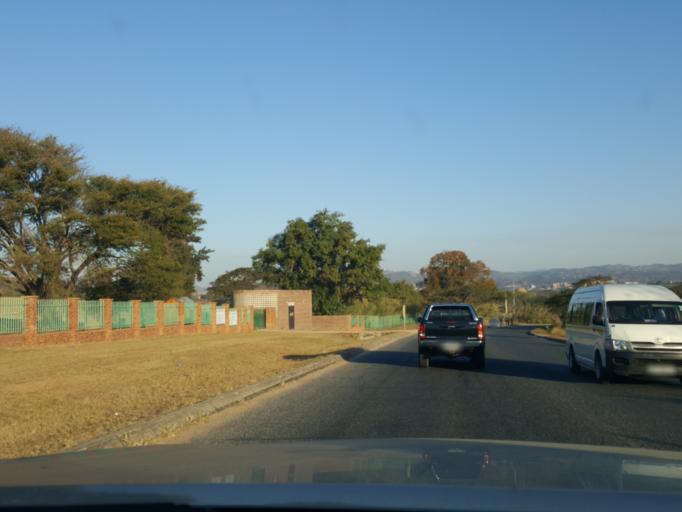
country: ZA
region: Mpumalanga
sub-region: Ehlanzeni District
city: Nelspruit
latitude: -25.4280
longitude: 30.9673
